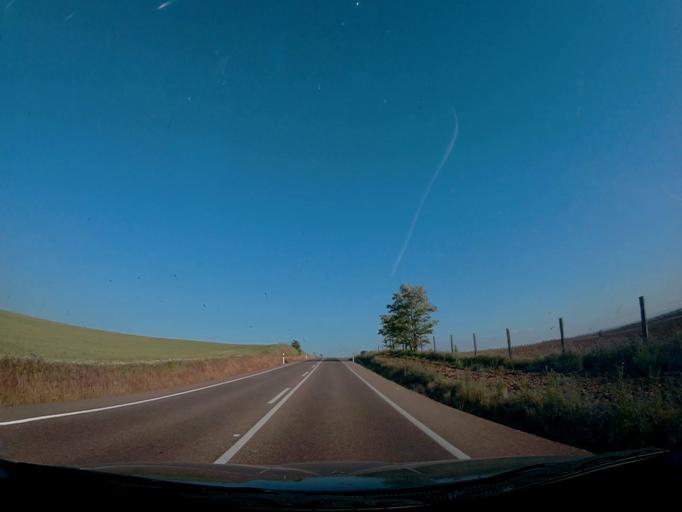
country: ES
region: Castille-La Mancha
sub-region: Province of Toledo
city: Maqueda
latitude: 40.1001
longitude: -4.3941
